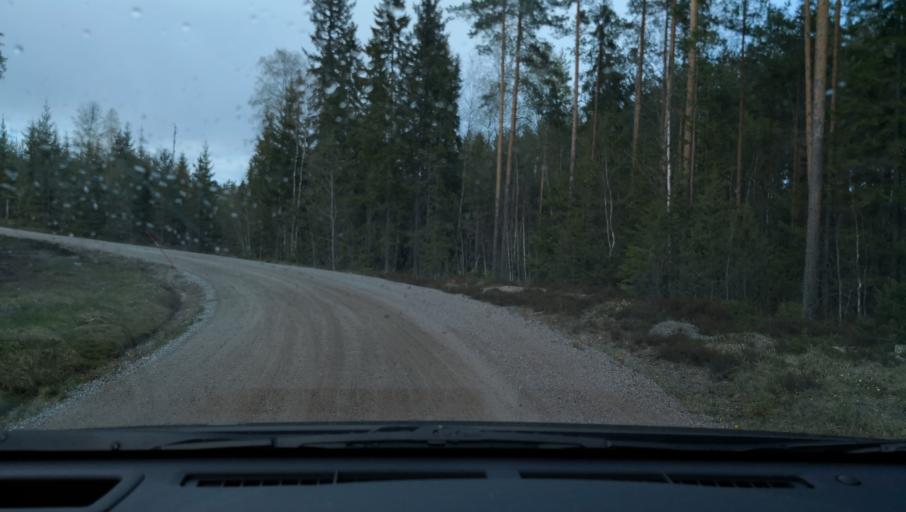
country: SE
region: Dalarna
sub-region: Saters Kommun
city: Saeter
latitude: 60.1725
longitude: 15.7257
